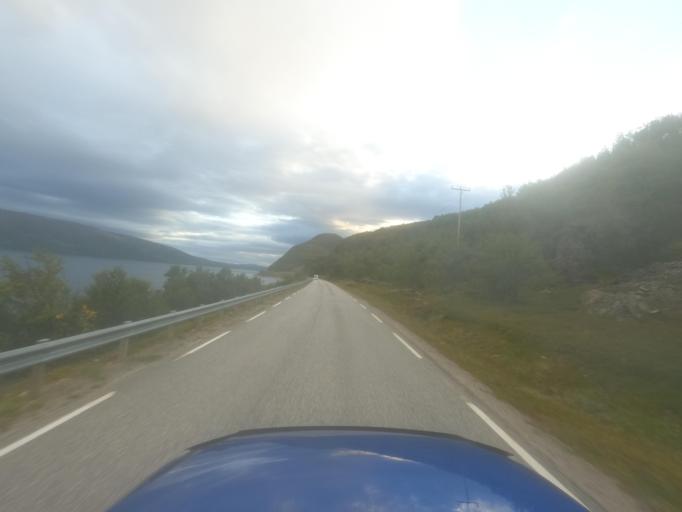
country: NO
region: Finnmark Fylke
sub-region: Porsanger
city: Lakselv
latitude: 70.5582
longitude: 25.1932
